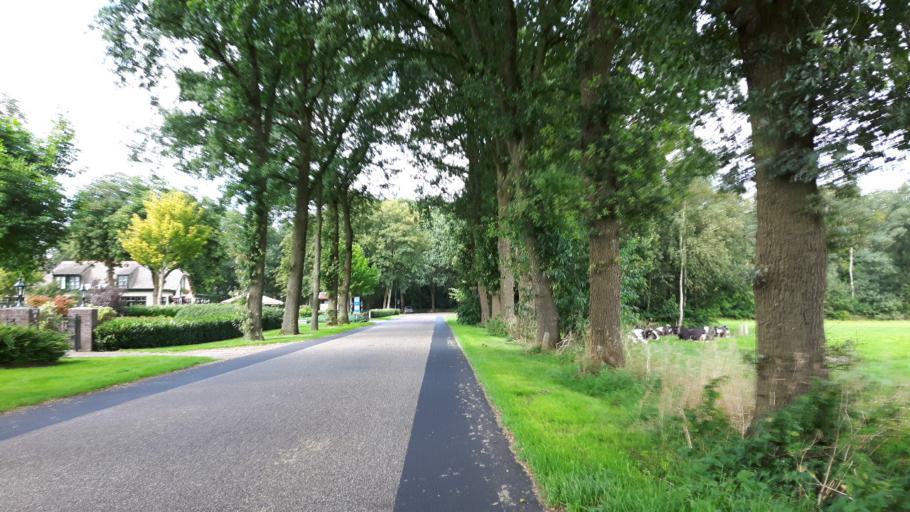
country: NL
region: Groningen
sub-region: Gemeente Leek
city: Leek
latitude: 53.0885
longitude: 6.3128
